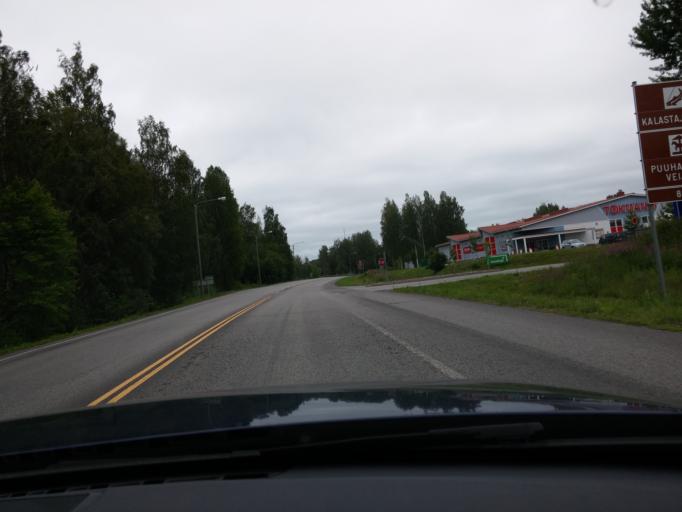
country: FI
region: Central Finland
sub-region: Saarijaervi-Viitasaari
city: Saarijaervi
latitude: 62.6998
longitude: 25.2798
